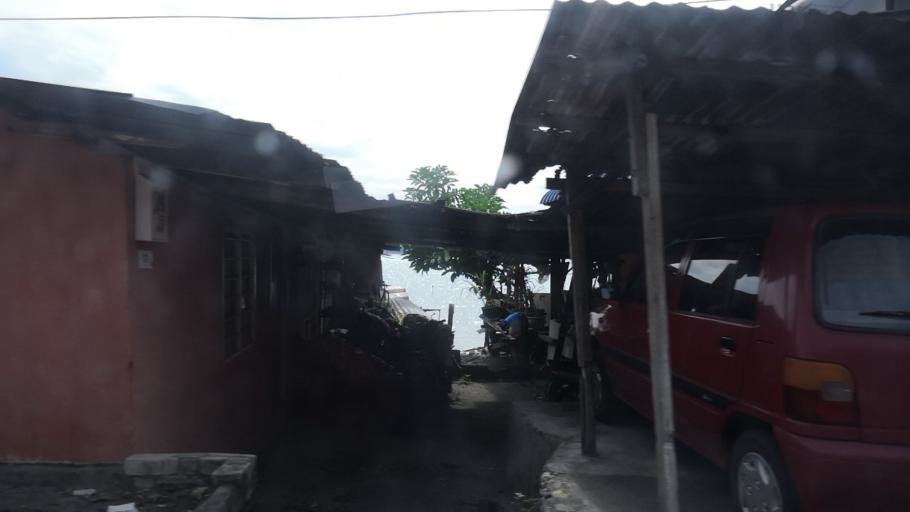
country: MY
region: Perak
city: Lumut
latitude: 4.1973
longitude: 100.5764
